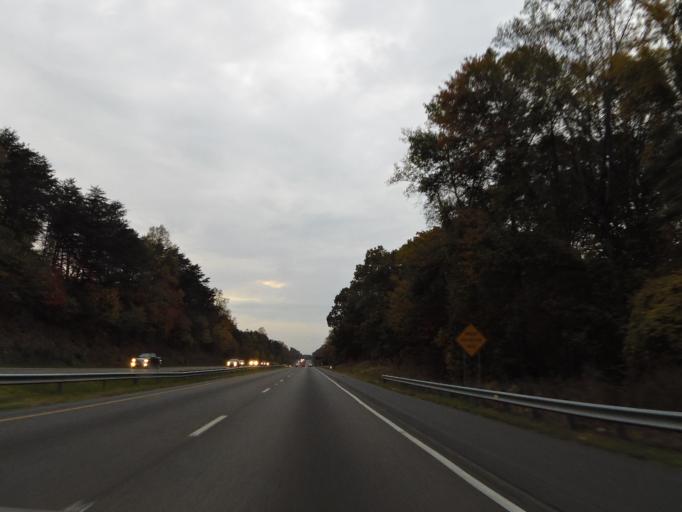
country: US
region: North Carolina
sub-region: Burke County
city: Icard
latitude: 35.7262
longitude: -81.4876
